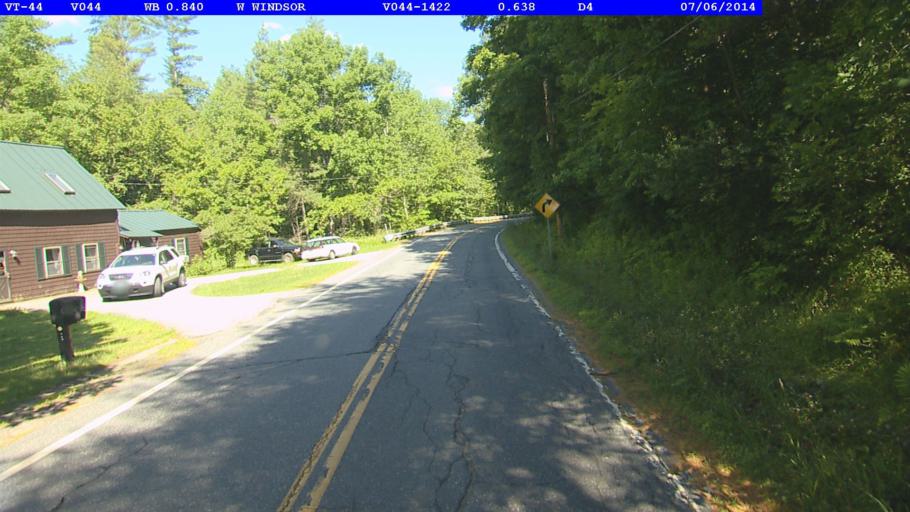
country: US
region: Vermont
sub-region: Windsor County
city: Windsor
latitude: 43.4638
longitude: -72.5228
